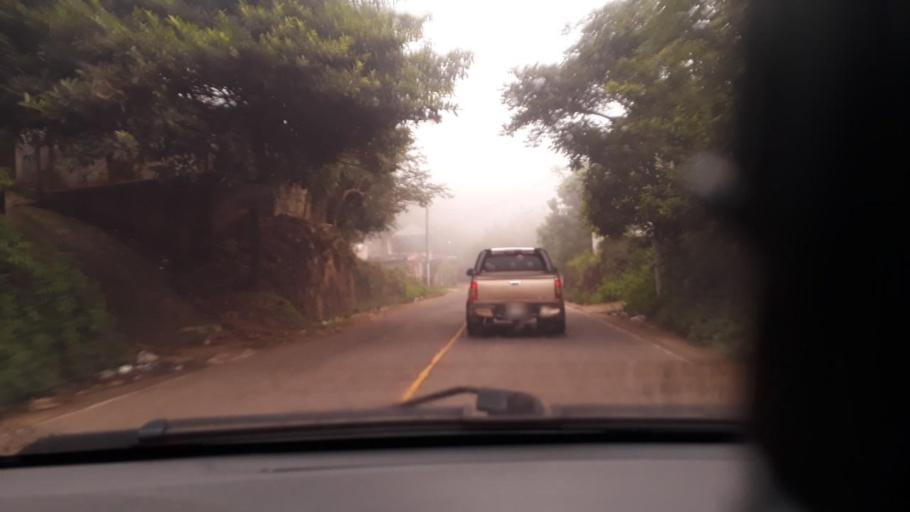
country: GT
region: Jutiapa
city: Jalpatagua
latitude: 14.1801
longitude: -90.0240
